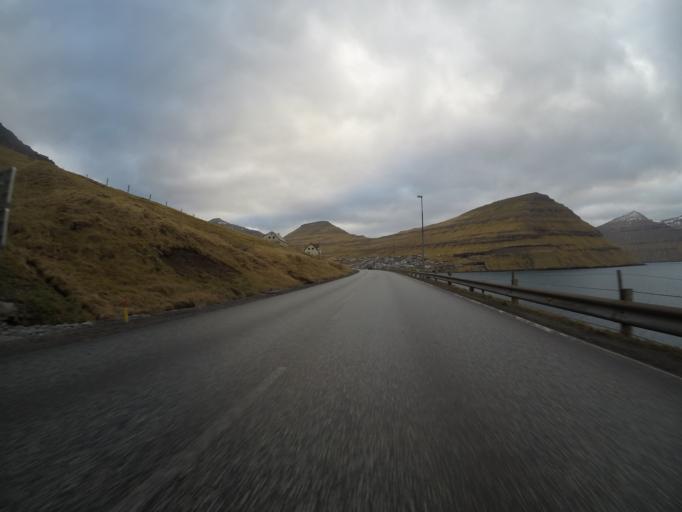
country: FO
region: Nordoyar
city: Klaksvik
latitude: 62.2450
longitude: -6.5880
